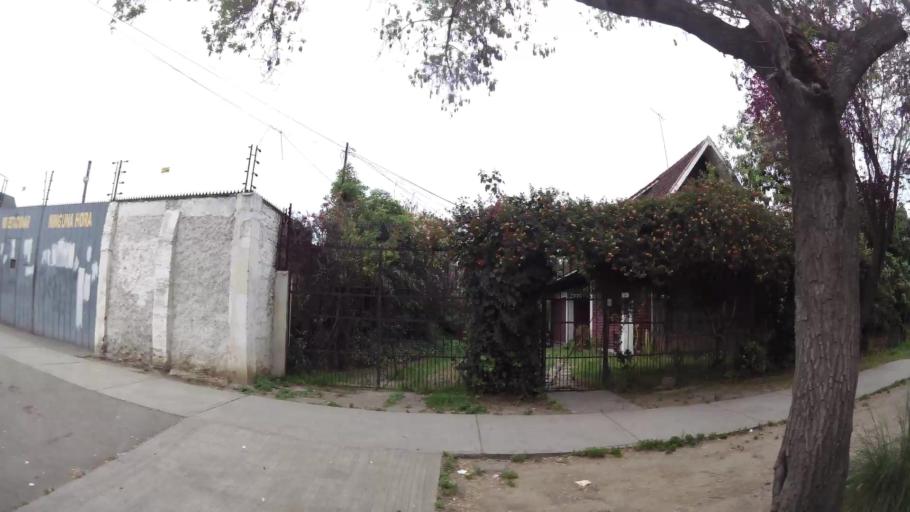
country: CL
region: Santiago Metropolitan
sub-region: Provincia de Santiago
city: Villa Presidente Frei, Nunoa, Santiago, Chile
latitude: -33.4804
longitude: -70.5886
